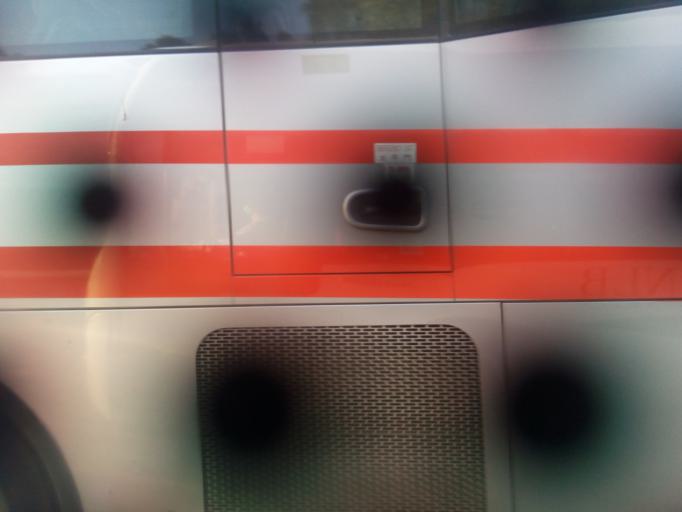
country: HK
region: Tuen Mun
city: Tuen Mun
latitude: 22.4251
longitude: 113.9984
